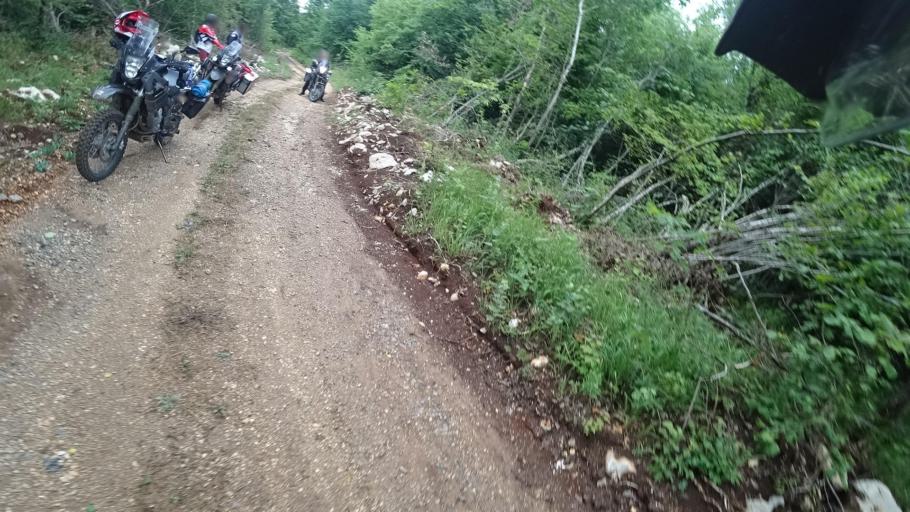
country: HR
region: Licko-Senjska
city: Jezerce
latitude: 44.7718
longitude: 15.4823
